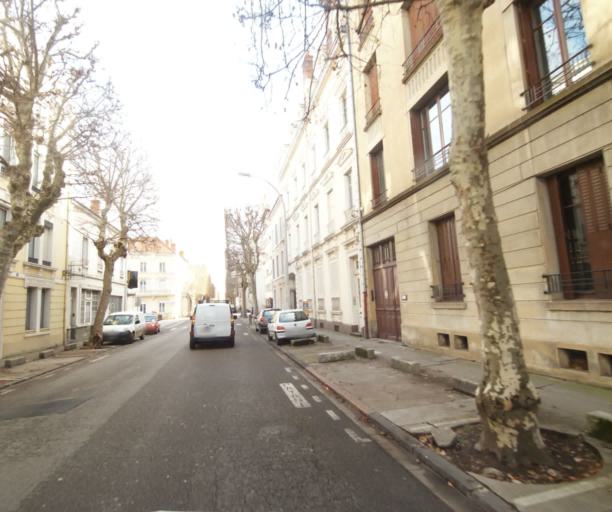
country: FR
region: Rhone-Alpes
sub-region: Departement de la Loire
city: Roanne
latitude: 46.0394
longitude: 4.0655
